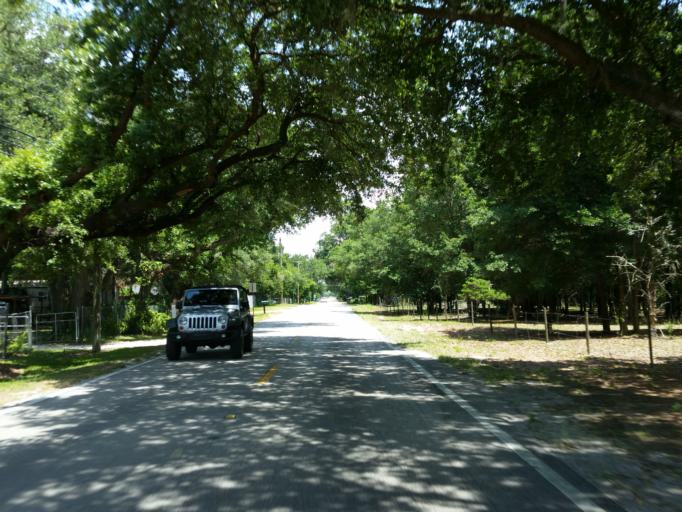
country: US
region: Florida
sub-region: Hillsborough County
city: Dover
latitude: 28.0470
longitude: -82.2051
